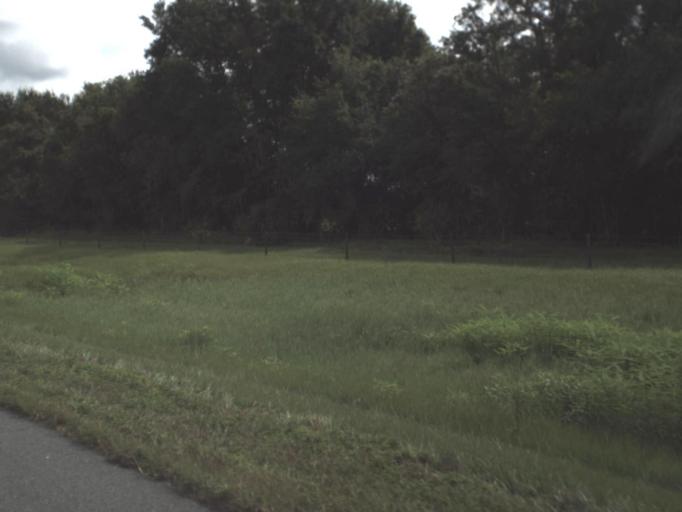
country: US
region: Florida
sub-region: Pasco County
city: Zephyrhills South
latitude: 28.1792
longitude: -82.2090
